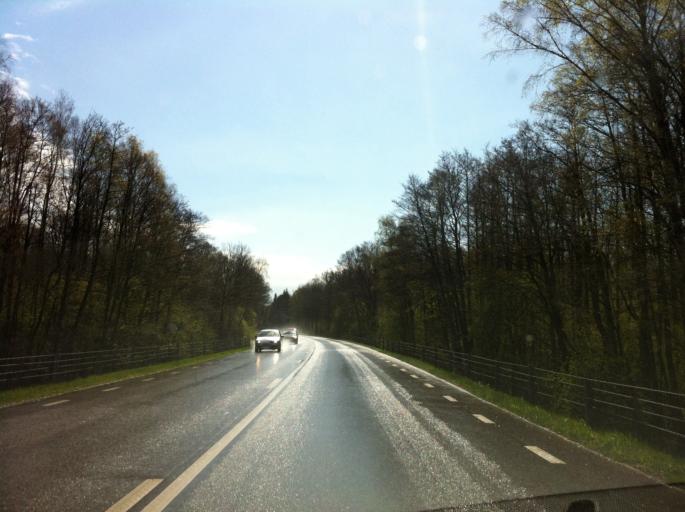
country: SE
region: Skane
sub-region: Hoors Kommun
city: Satofta
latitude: 55.9020
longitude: 13.6125
